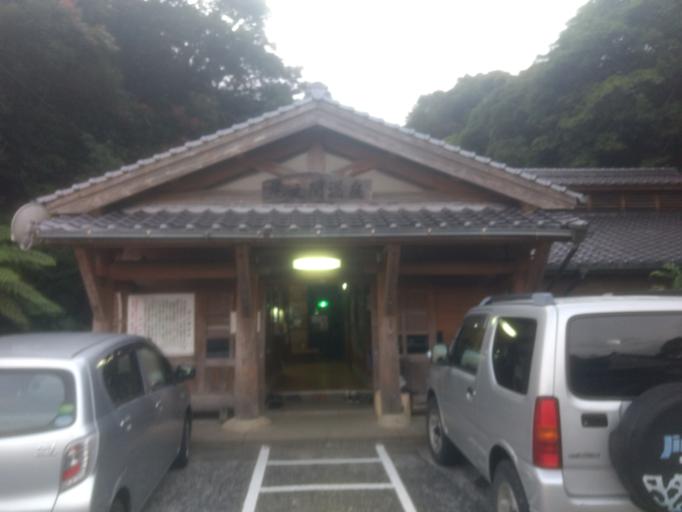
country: JP
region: Kagoshima
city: Nishinoomote
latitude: 30.2403
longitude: 130.5488
